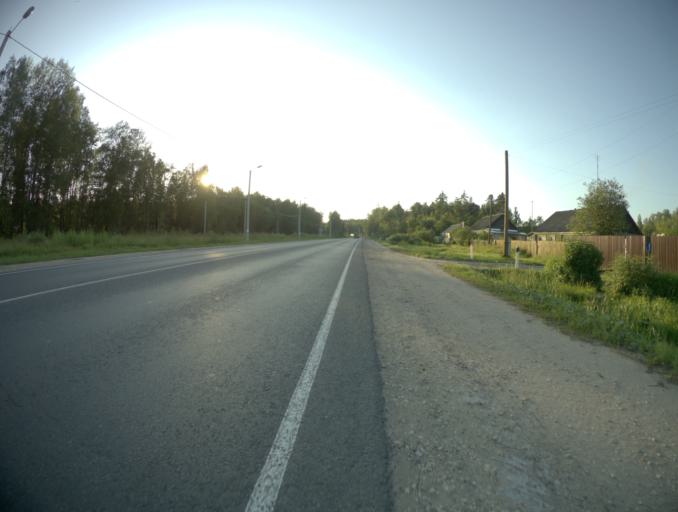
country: RU
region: Vladimir
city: Kommunar
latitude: 56.0514
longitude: 40.5295
